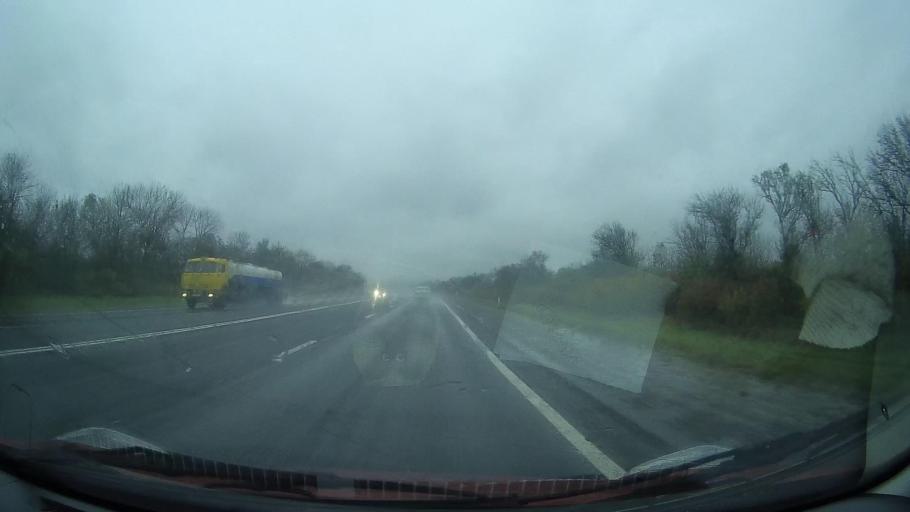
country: RU
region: Stavropol'skiy
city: Nevinnomyssk
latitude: 44.6189
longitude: 42.0957
